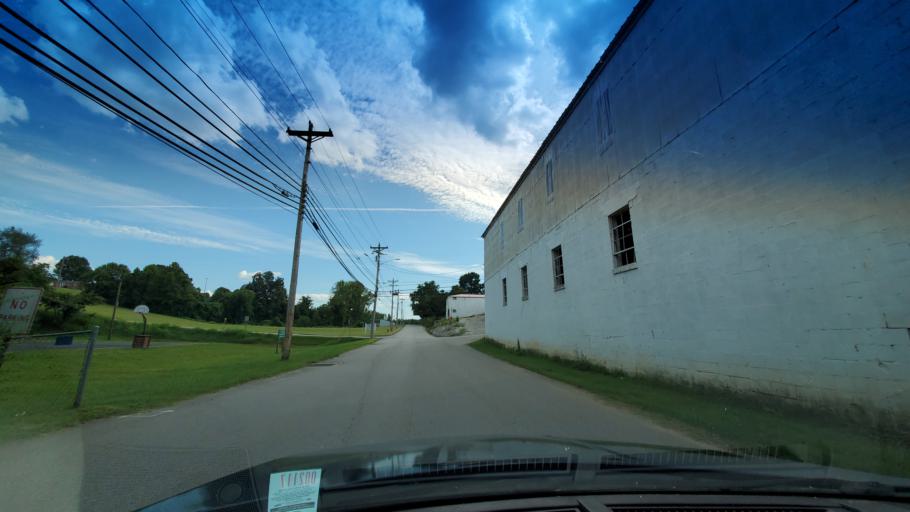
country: US
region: Tennessee
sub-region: Smith County
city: Carthage
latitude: 36.2504
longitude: -85.9511
